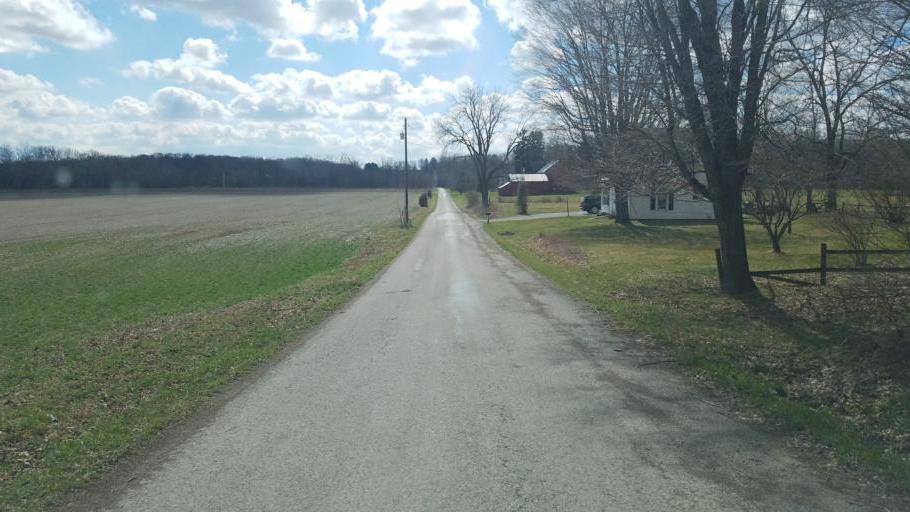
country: US
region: Ohio
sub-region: Knox County
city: Fredericktown
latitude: 40.5081
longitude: -82.5711
